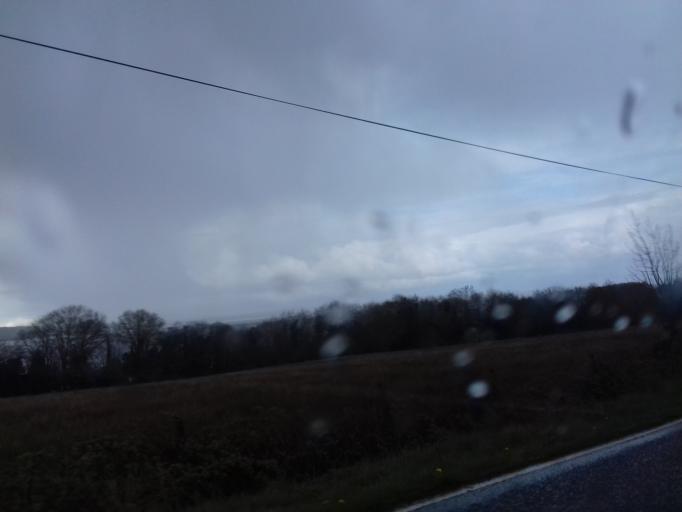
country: IE
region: Ulster
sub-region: County Donegal
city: Ballyshannon
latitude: 54.4725
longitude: -7.9289
